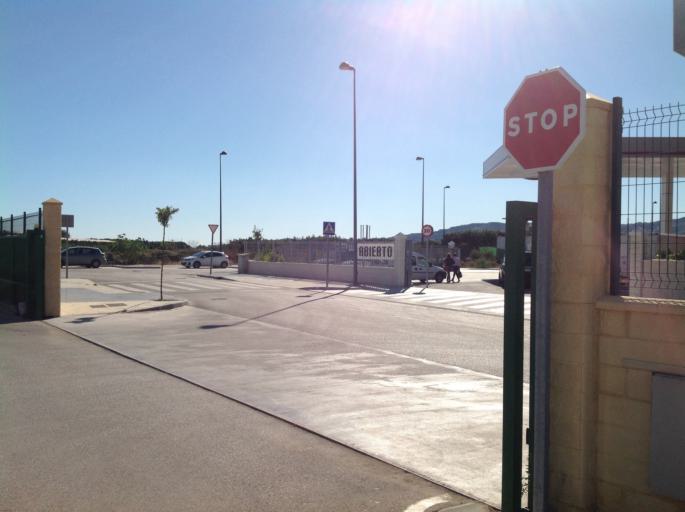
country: ES
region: Andalusia
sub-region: Provincia de Malaga
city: Velez-Malaga
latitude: 36.7989
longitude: -4.1177
